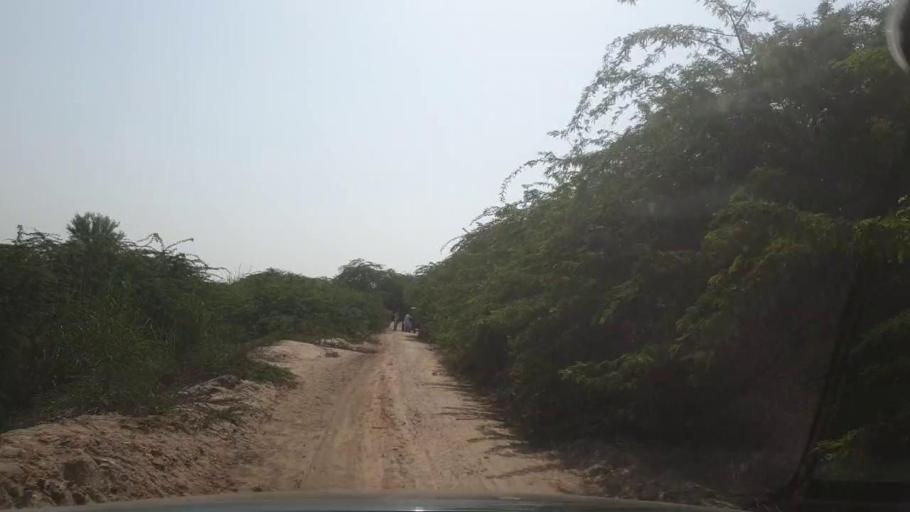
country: PK
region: Sindh
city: Naukot
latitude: 24.7962
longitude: 69.2467
